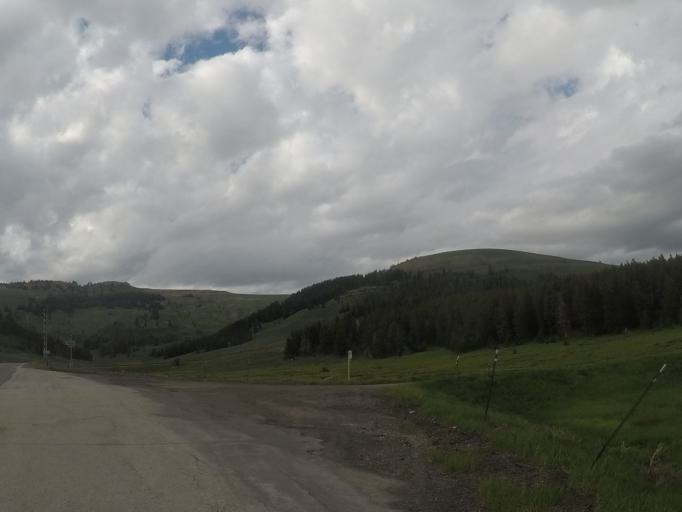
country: US
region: Wyoming
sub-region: Big Horn County
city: Greybull
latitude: 44.6138
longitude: -107.5215
